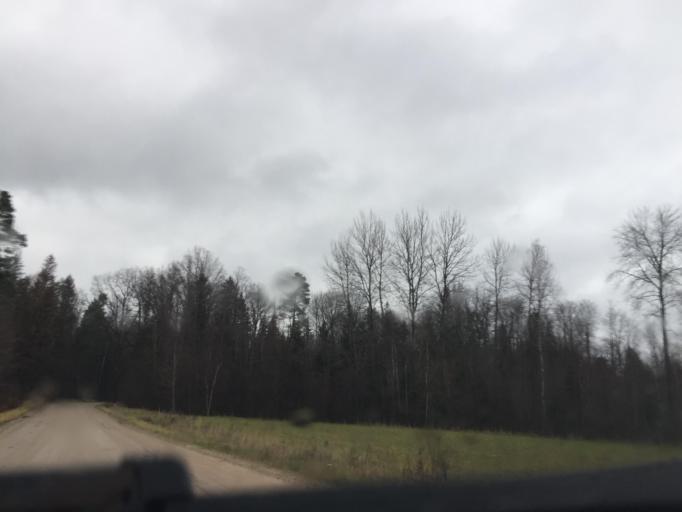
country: LV
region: Limbazu Rajons
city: Limbazi
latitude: 57.6447
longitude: 24.7755
